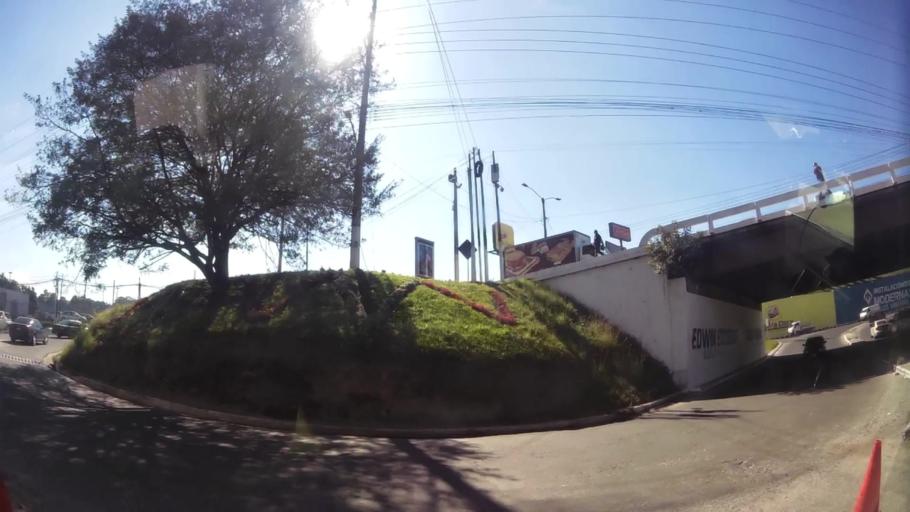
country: GT
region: Guatemala
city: Villa Nueva
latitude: 14.5306
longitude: -90.5956
